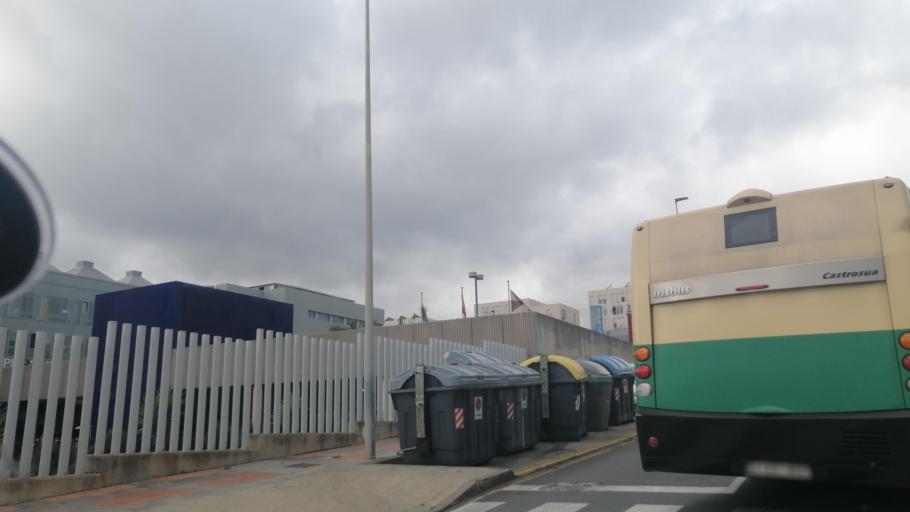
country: ES
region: Ceuta
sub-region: Ceuta
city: Ceuta
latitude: 35.8811
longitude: -5.3408
